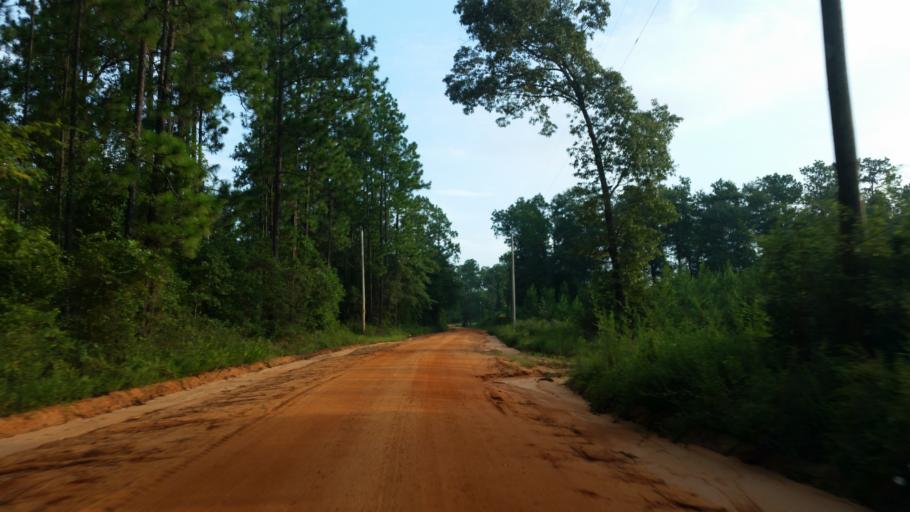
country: US
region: Alabama
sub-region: Escambia County
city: Atmore
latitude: 30.8470
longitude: -87.5764
